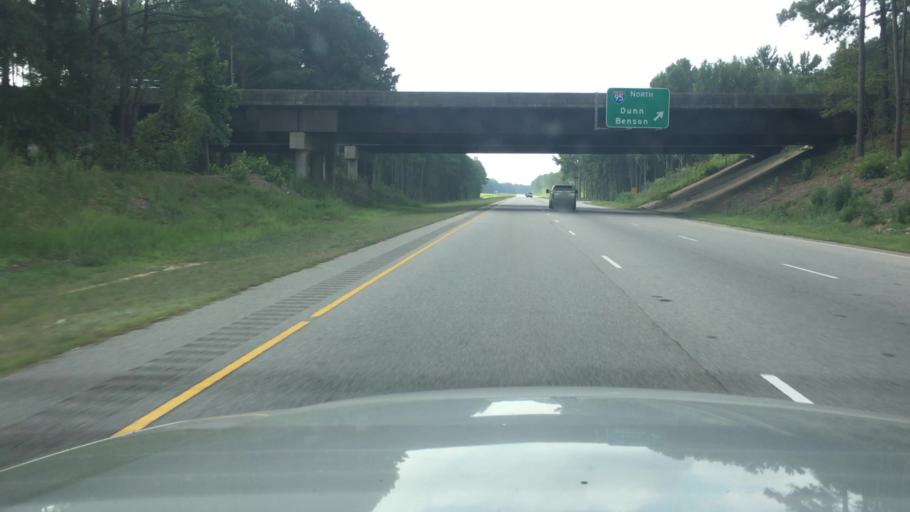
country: US
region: North Carolina
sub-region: Cumberland County
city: Fayetteville
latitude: 34.9767
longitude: -78.8571
